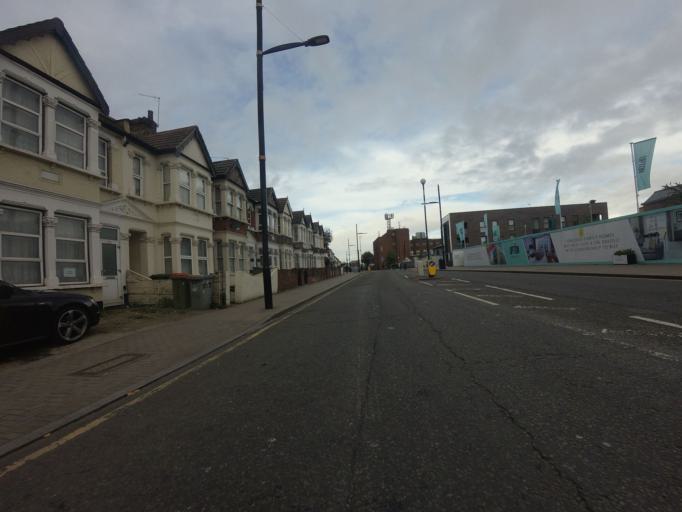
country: GB
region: England
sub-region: Greater London
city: East Ham
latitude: 51.5319
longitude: 0.0373
